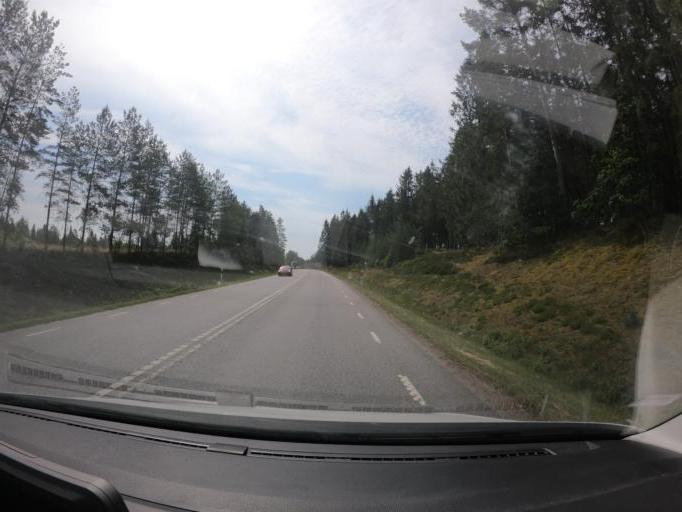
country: SE
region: Skane
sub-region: Hassleholms Kommun
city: Bjarnum
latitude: 56.2330
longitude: 13.7140
